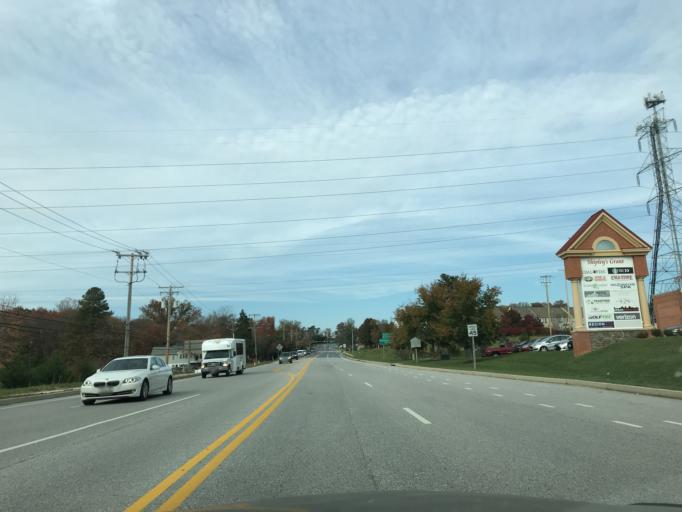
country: US
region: Maryland
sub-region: Howard County
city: Columbia
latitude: 39.2135
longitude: -76.8027
